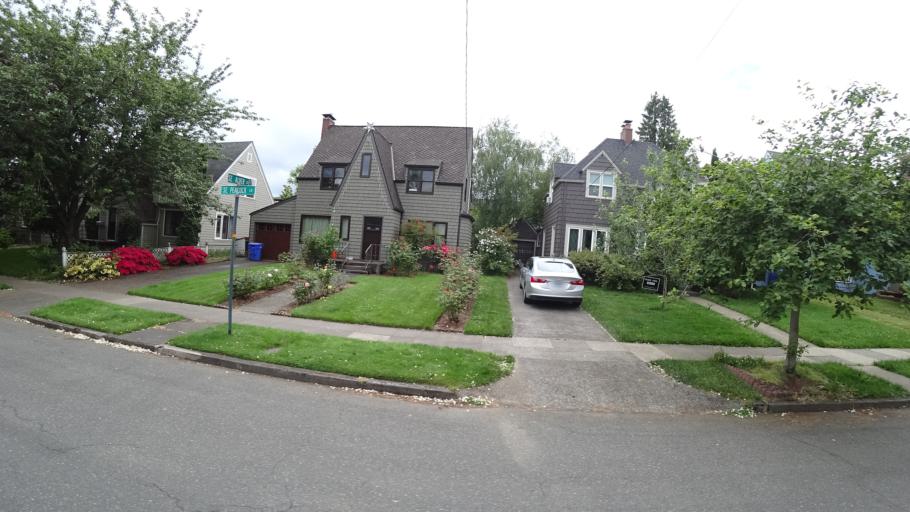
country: US
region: Oregon
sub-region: Multnomah County
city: Portland
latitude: 45.5179
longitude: -122.6217
